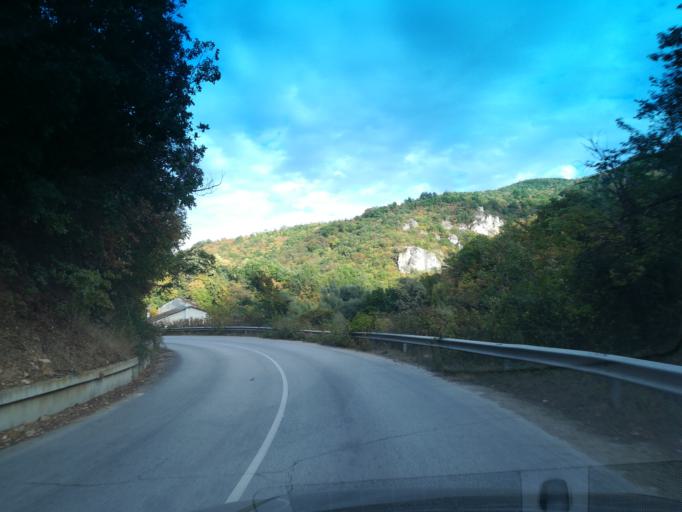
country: BG
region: Pazardzhik
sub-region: Obshtina Peshtera
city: Peshtera
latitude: 42.0173
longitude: 24.2775
